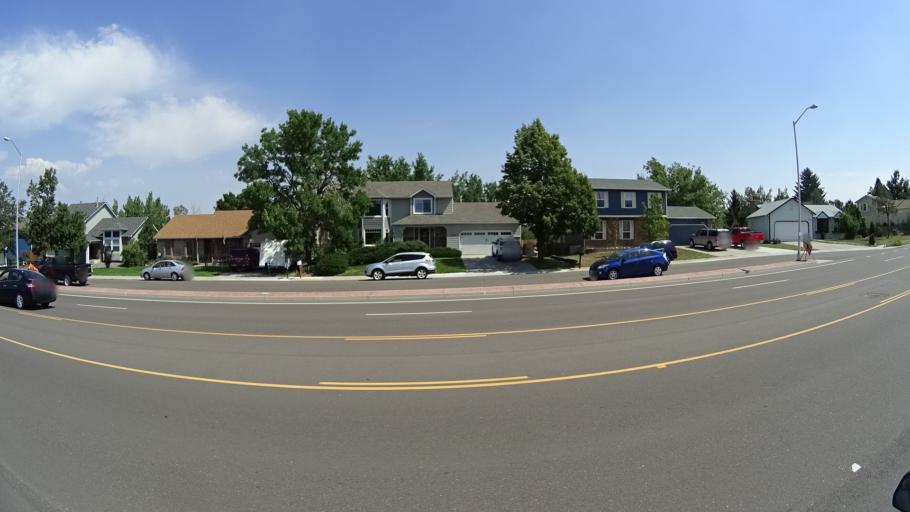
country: US
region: Colorado
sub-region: El Paso County
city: Cimarron Hills
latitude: 38.9256
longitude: -104.7715
